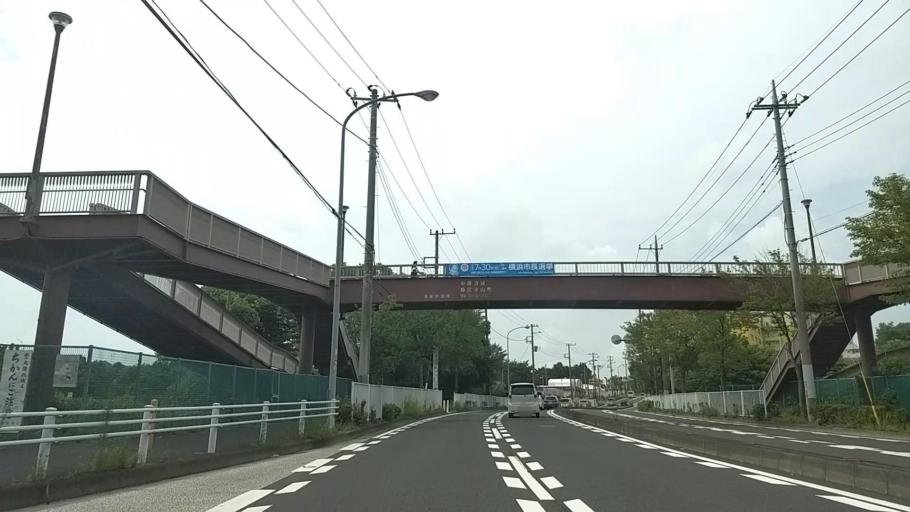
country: JP
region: Kanagawa
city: Minami-rinkan
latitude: 35.5042
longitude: 139.5433
